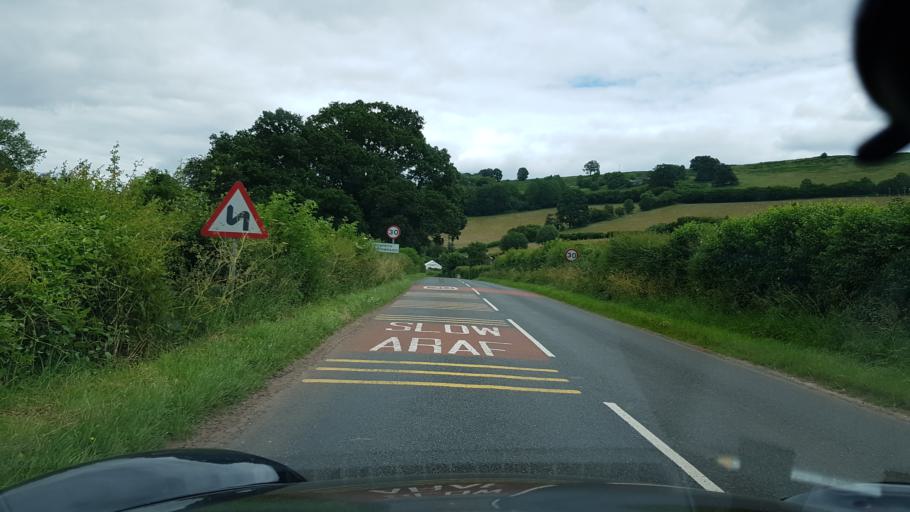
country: GB
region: England
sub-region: Herefordshire
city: Llanrothal
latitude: 51.8778
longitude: -2.7932
